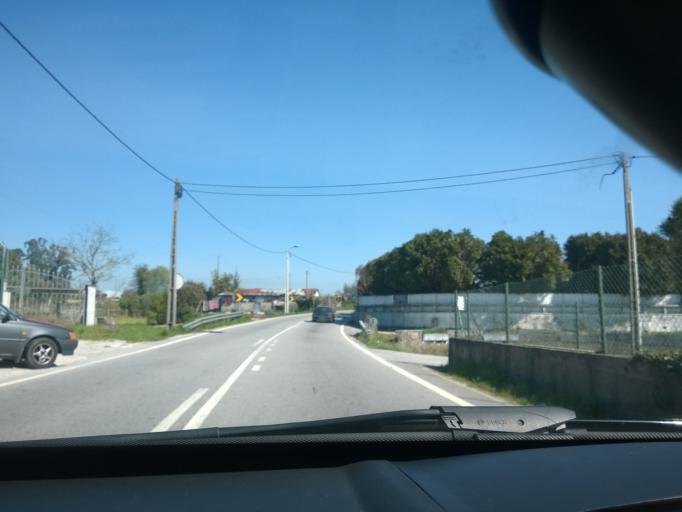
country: PT
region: Porto
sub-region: Penafiel
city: Penafiel
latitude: 41.1864
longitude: -8.3046
